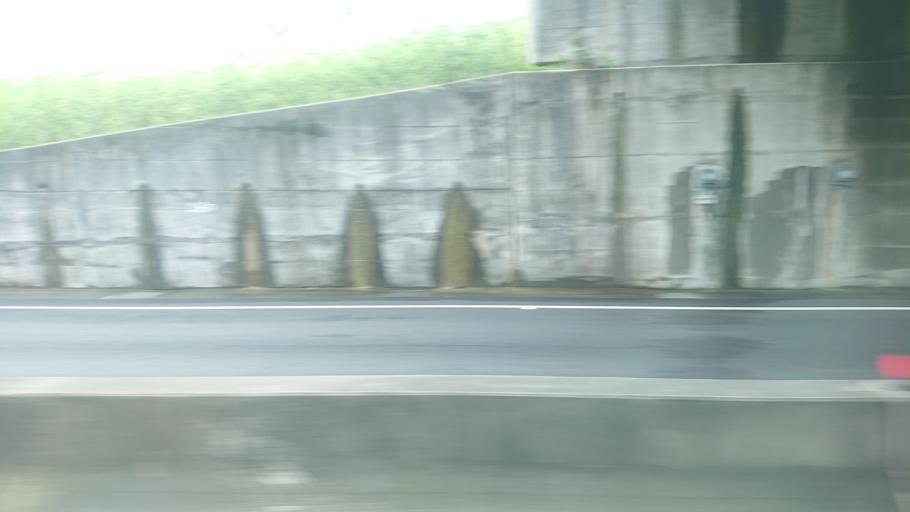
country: TW
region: Taiwan
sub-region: Keelung
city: Keelung
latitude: 25.0866
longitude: 121.6871
